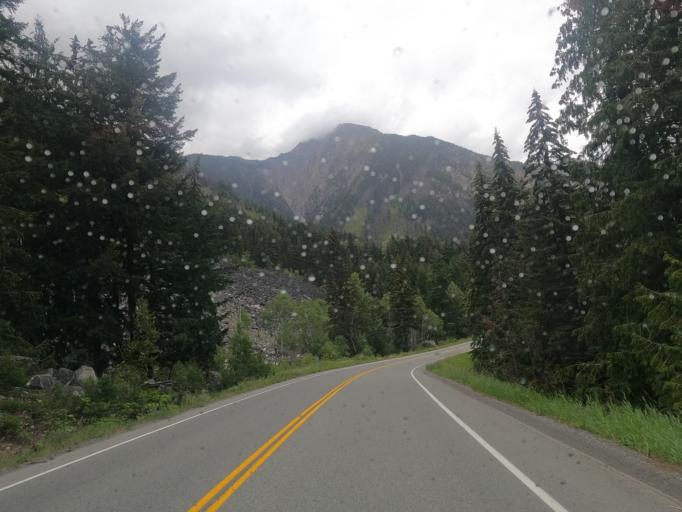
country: CA
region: British Columbia
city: Lillooet
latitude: 50.5269
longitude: -122.1610
